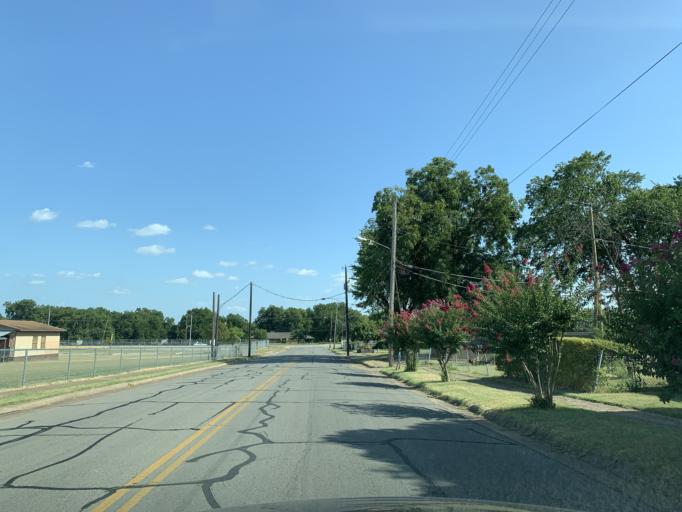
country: US
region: Texas
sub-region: Dallas County
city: Hutchins
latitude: 32.6908
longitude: -96.7838
